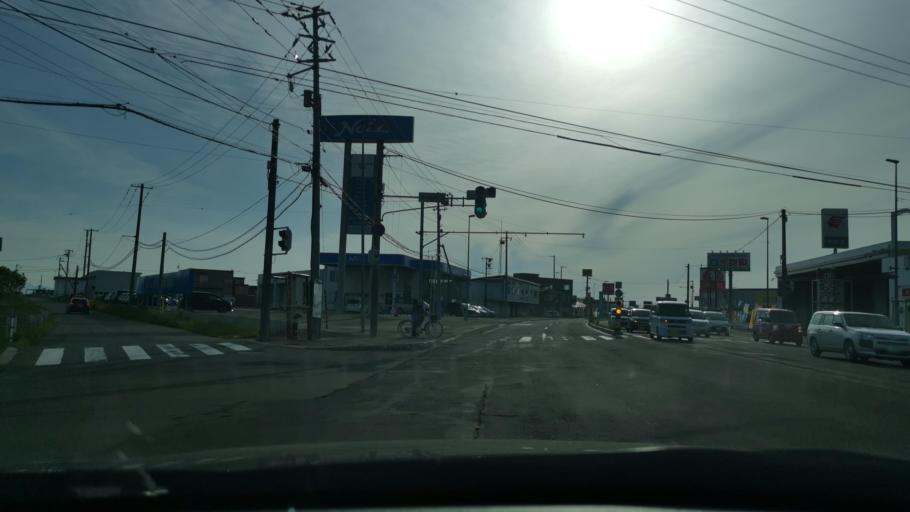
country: JP
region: Hokkaido
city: Iwamizawa
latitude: 43.1864
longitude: 141.7415
